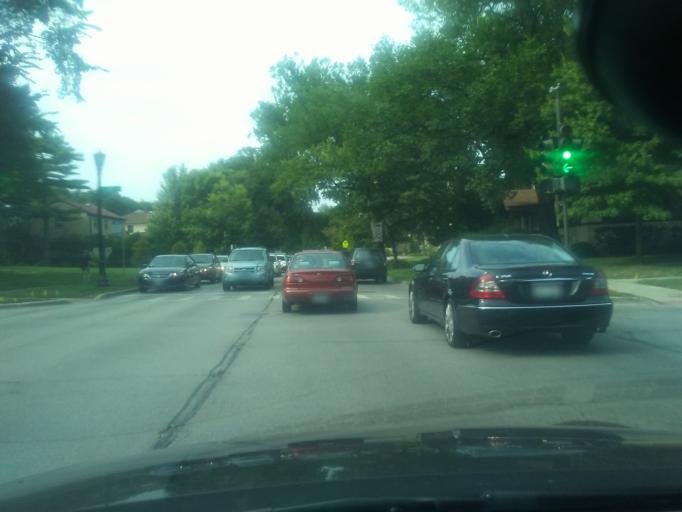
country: US
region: Illinois
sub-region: Cook County
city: Evanston
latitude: 42.0442
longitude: -87.6885
